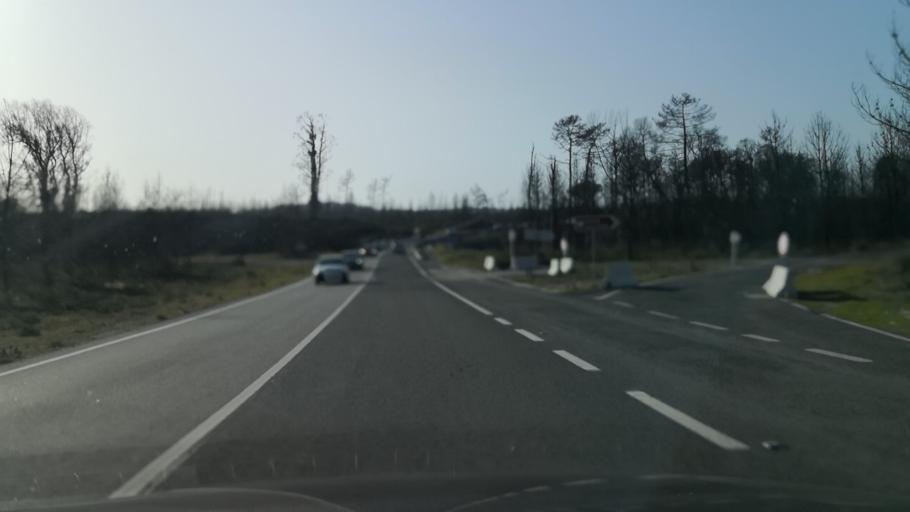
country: PT
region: Leiria
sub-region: Marinha Grande
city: Marinha Grande
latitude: 39.7467
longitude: -8.9733
